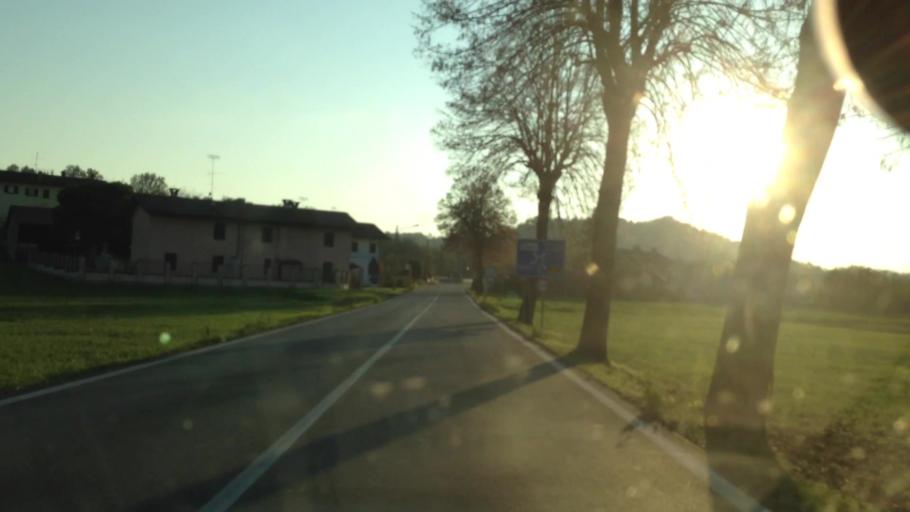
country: IT
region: Piedmont
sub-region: Provincia di Torino
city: Brusasco
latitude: 45.1596
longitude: 8.0762
